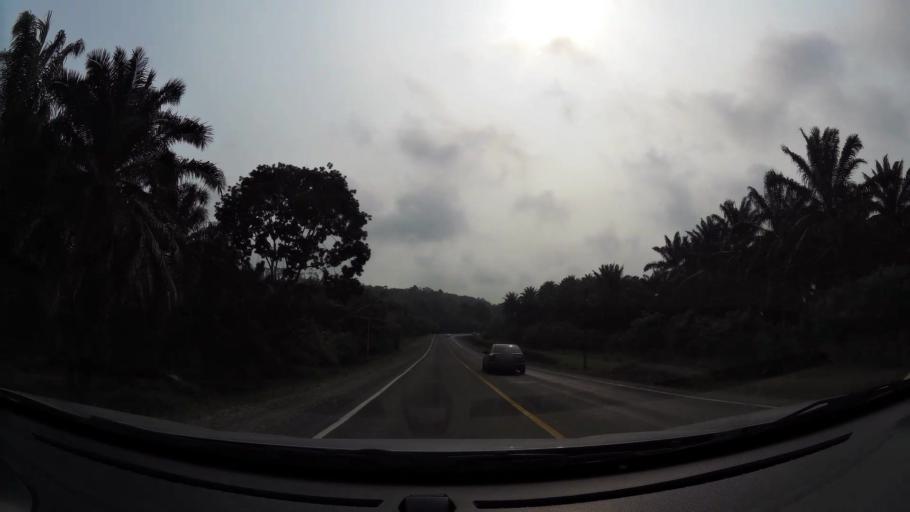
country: HN
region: Yoro
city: Toyos
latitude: 15.5539
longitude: -87.6452
